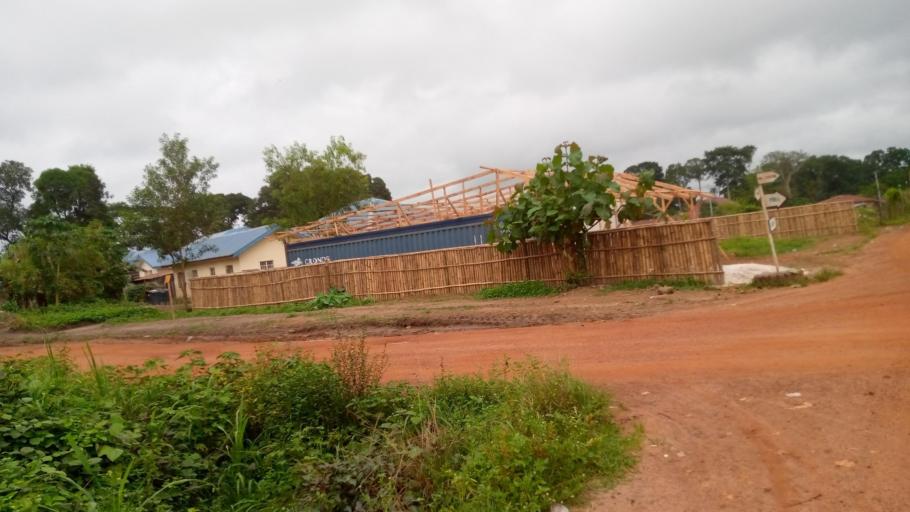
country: SL
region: Southern Province
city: Tongole
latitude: 7.4365
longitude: -11.8439
